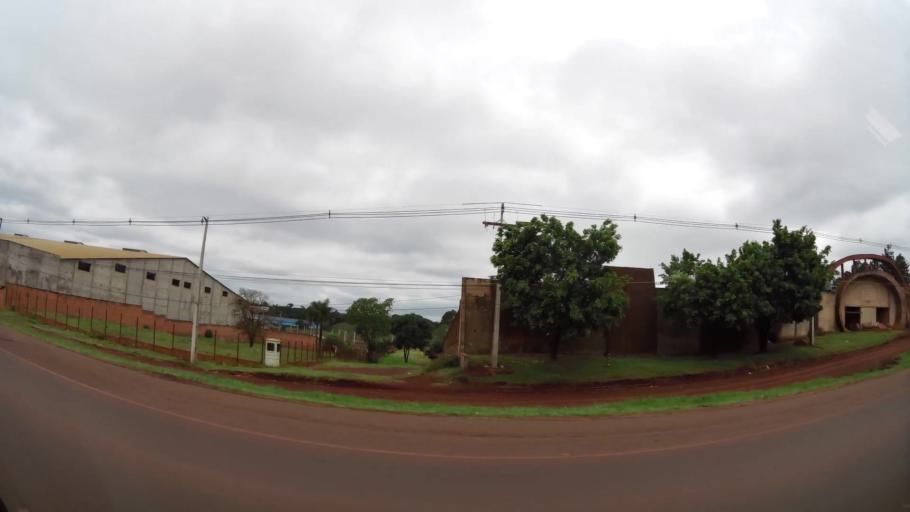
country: PY
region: Alto Parana
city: Ciudad del Este
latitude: -25.4938
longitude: -54.7159
